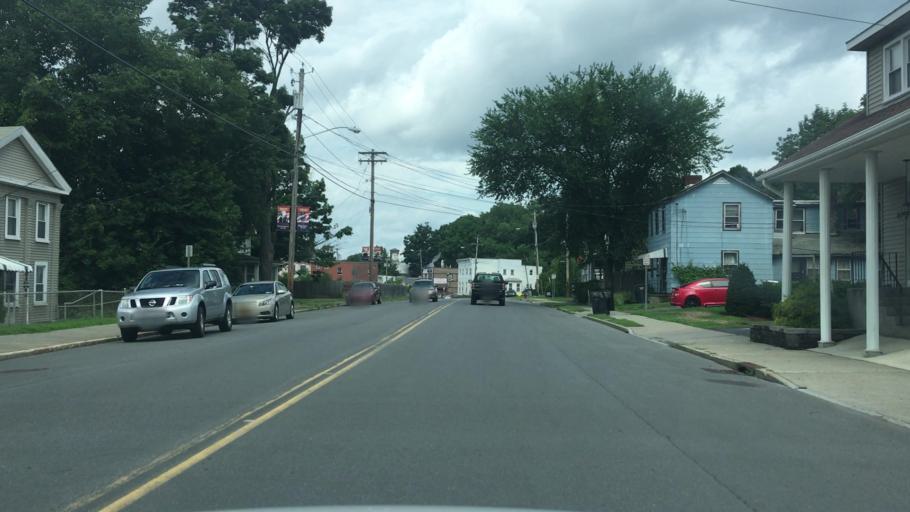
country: US
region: New York
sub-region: Rensselaer County
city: Wynantskill
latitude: 42.7005
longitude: -73.6534
